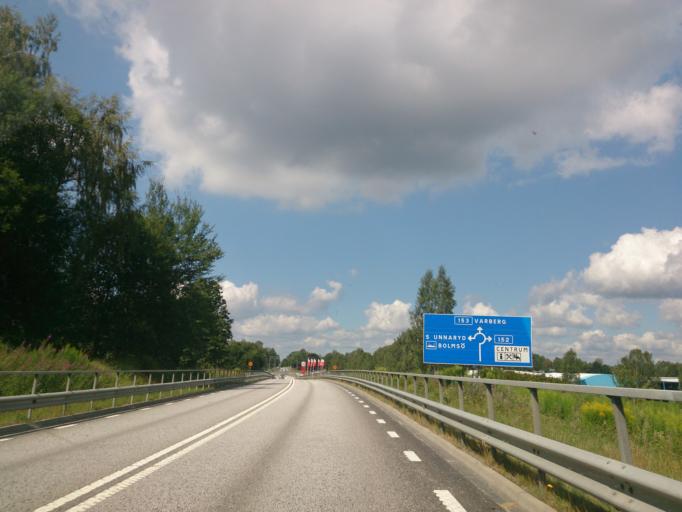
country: SE
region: Joenkoeping
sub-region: Varnamo Kommun
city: Bredaryd
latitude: 57.1716
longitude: 13.7464
